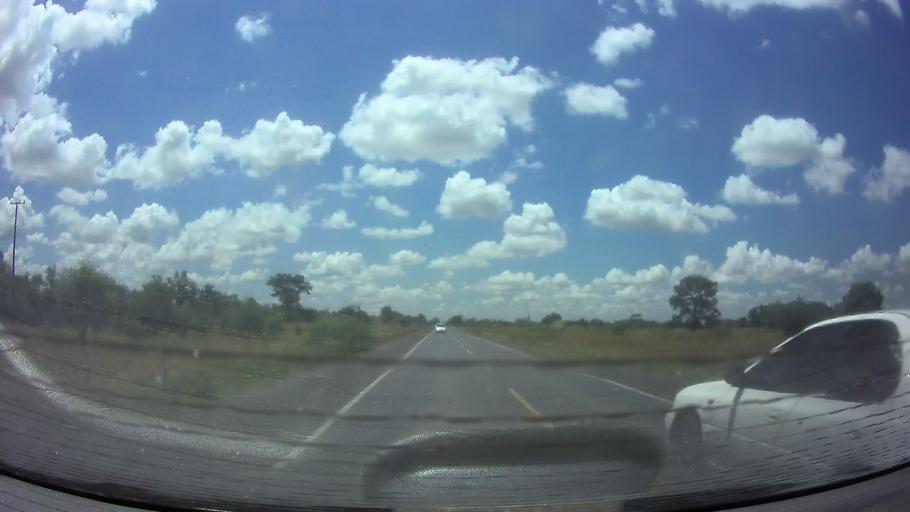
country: PY
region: Presidente Hayes
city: Nanawa
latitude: -25.2224
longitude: -57.6797
